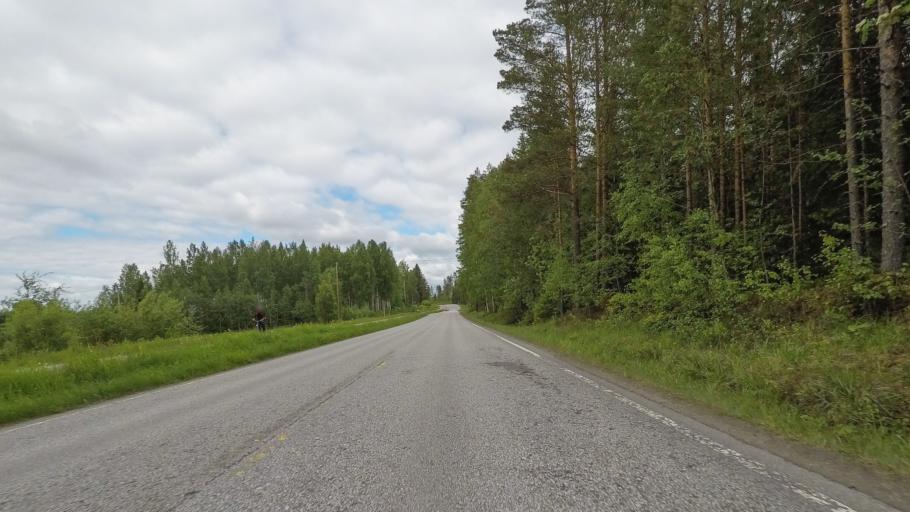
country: FI
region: Central Finland
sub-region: Jyvaeskylae
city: Toivakka
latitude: 62.0856
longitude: 26.0607
